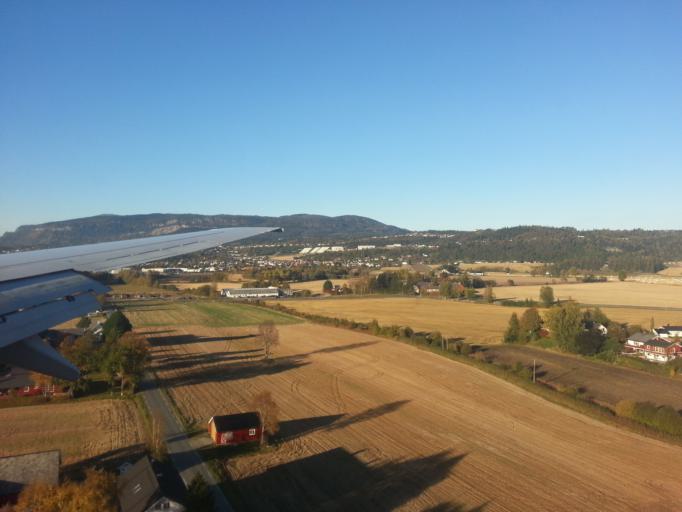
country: NO
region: Nord-Trondelag
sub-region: Stjordal
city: Stjordalshalsen
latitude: 63.4575
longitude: 10.9511
